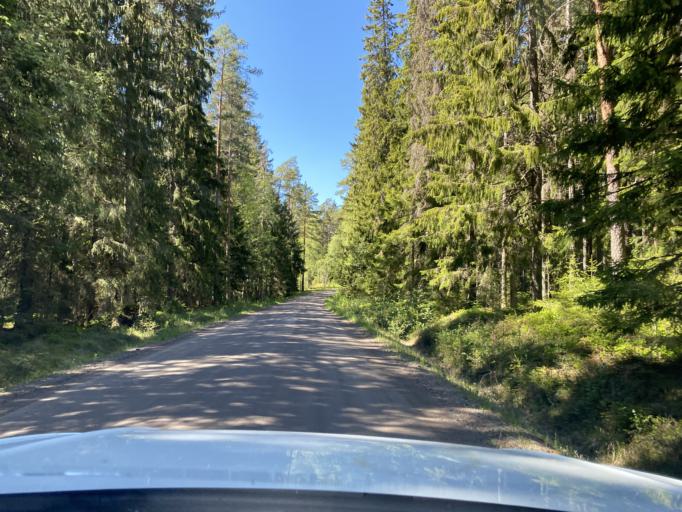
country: FI
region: Satakunta
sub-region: Rauma
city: Kiukainen
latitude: 61.1359
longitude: 21.9731
